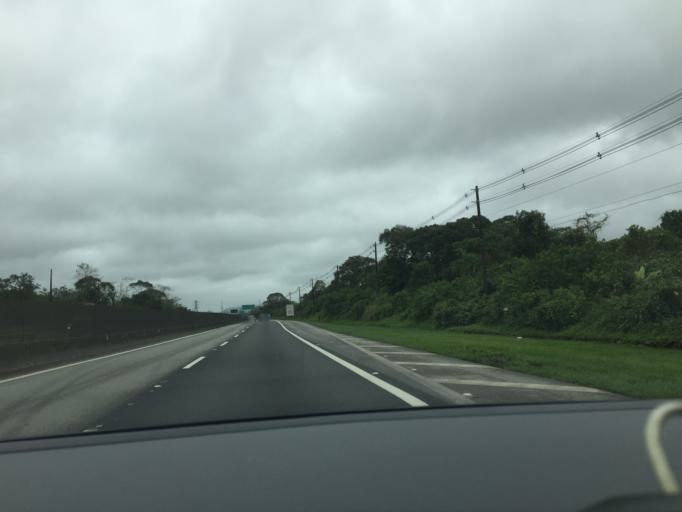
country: BR
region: Sao Paulo
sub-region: Santos
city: Santos
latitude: -23.9272
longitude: -46.2852
